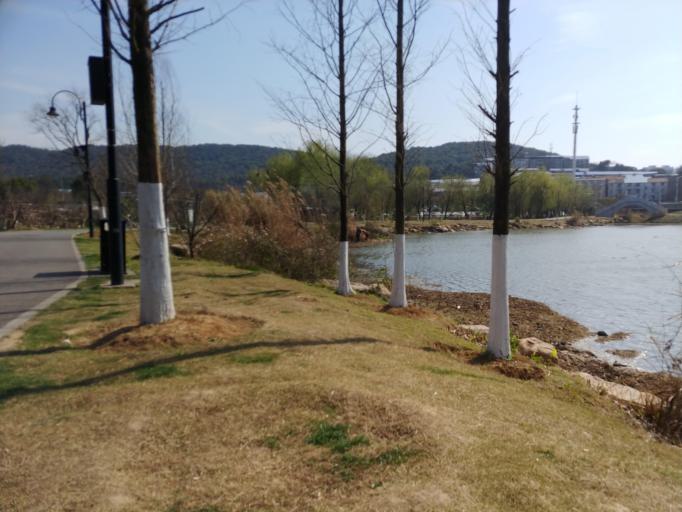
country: CN
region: Hubei
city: Guanshan
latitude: 30.5328
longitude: 114.4019
